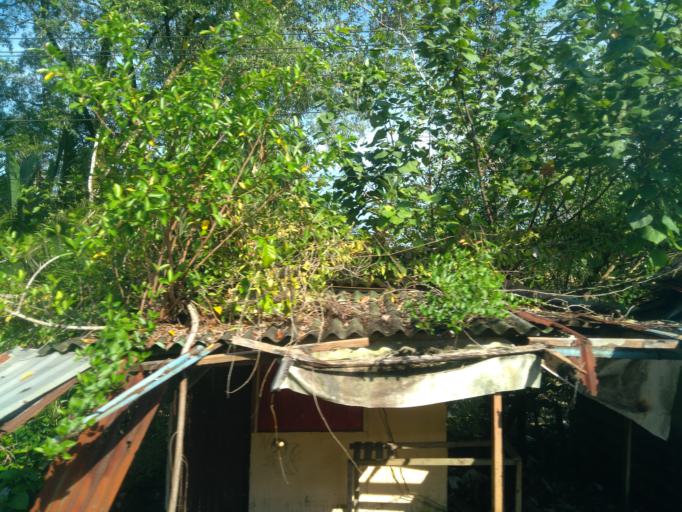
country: MY
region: Sarawak
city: Kuching
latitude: 1.6631
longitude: 110.4321
